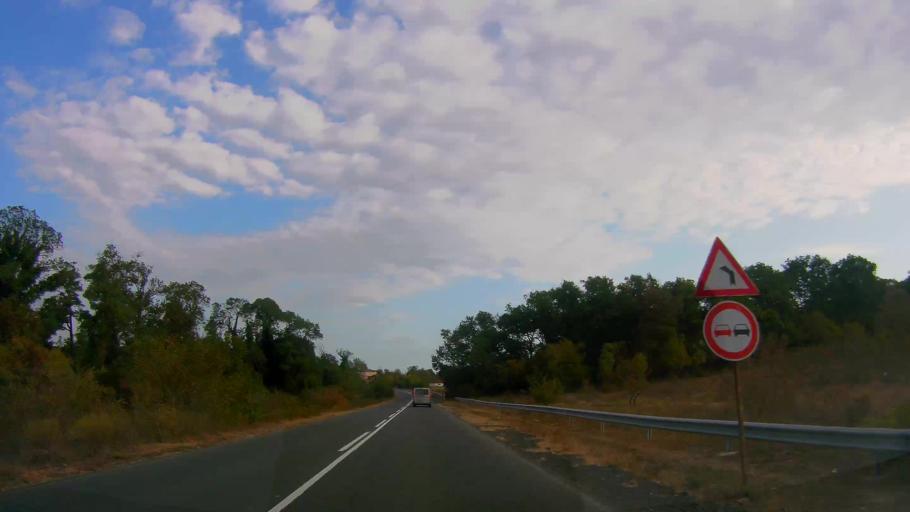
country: BG
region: Burgas
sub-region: Obshtina Primorsko
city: Primorsko
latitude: 42.3249
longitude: 27.7305
